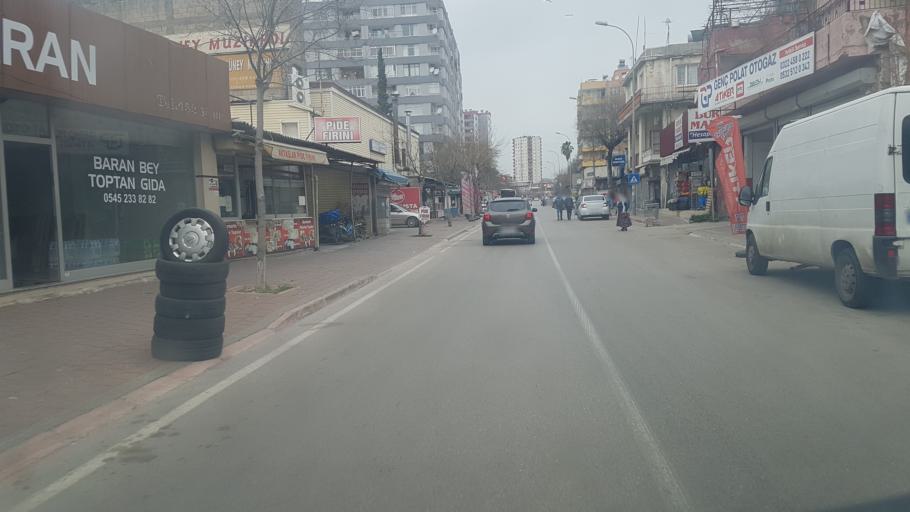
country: TR
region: Adana
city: Seyhan
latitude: 37.0064
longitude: 35.3099
